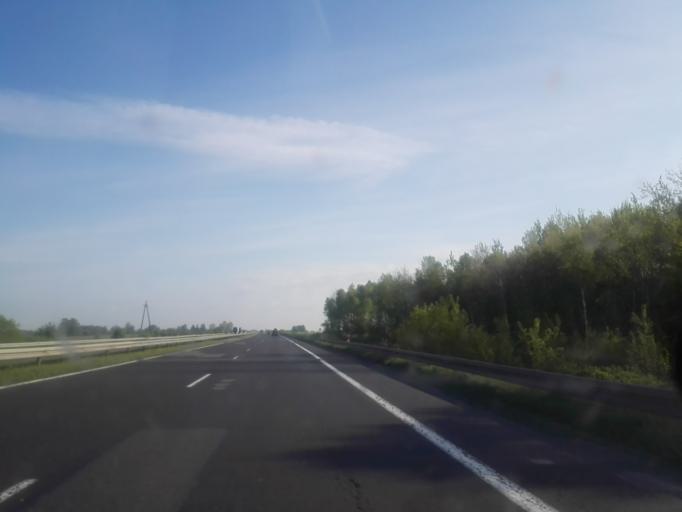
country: PL
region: Lodz Voivodeship
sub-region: Powiat radomszczanski
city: Kamiensk
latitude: 51.2548
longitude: 19.5278
